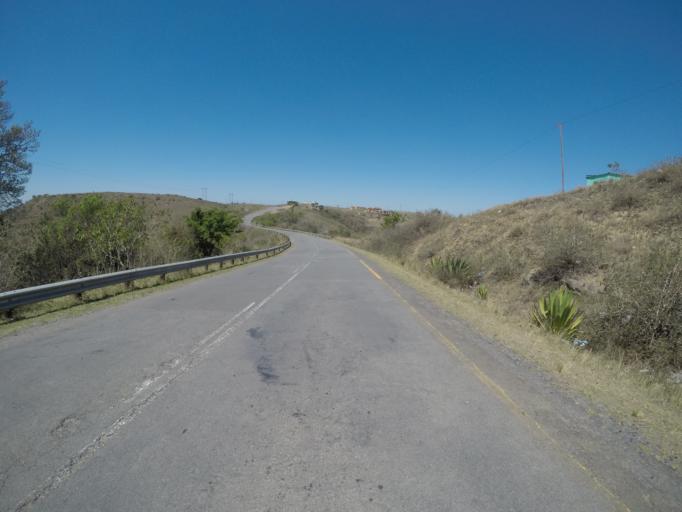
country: ZA
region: Eastern Cape
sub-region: OR Tambo District Municipality
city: Mthatha
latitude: -31.9097
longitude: 28.9527
